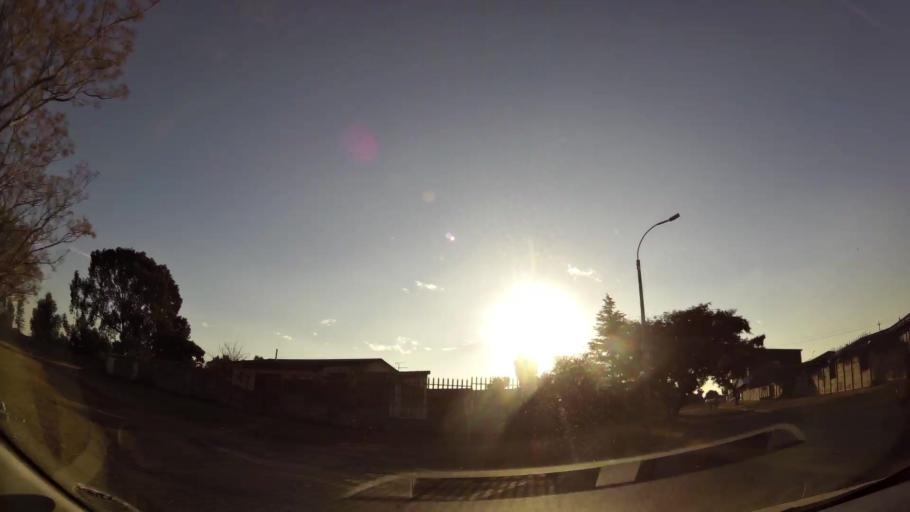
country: ZA
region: Gauteng
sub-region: West Rand District Municipality
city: Randfontein
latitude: -26.2234
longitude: 27.6451
